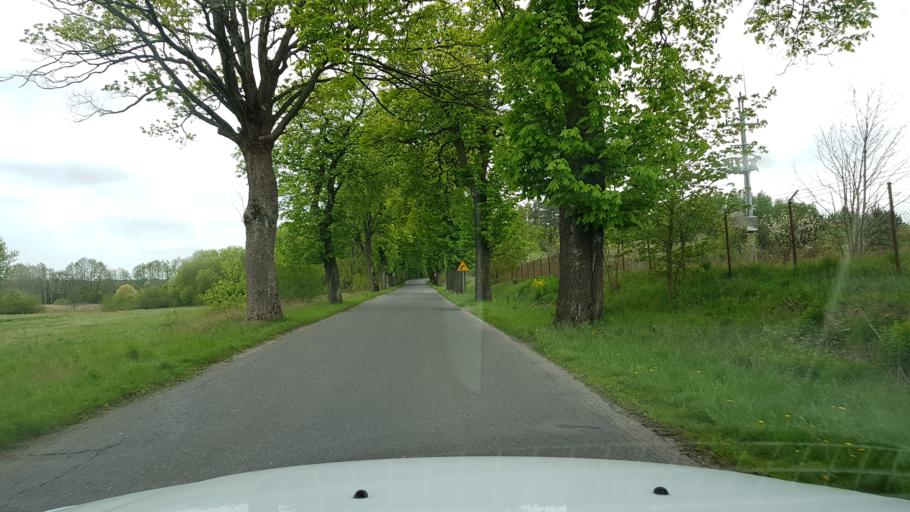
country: PL
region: West Pomeranian Voivodeship
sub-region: Powiat slawienski
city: Slawno
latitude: 54.3842
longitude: 16.6961
